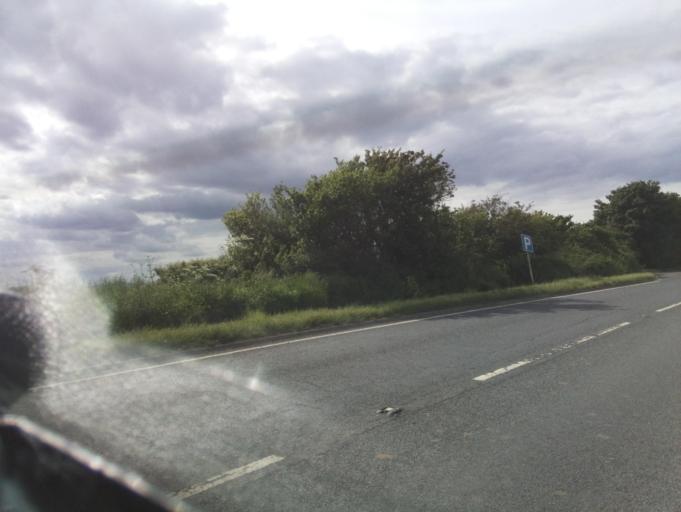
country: GB
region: England
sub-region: Worcestershire
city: Pershore
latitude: 52.1213
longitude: -2.1025
